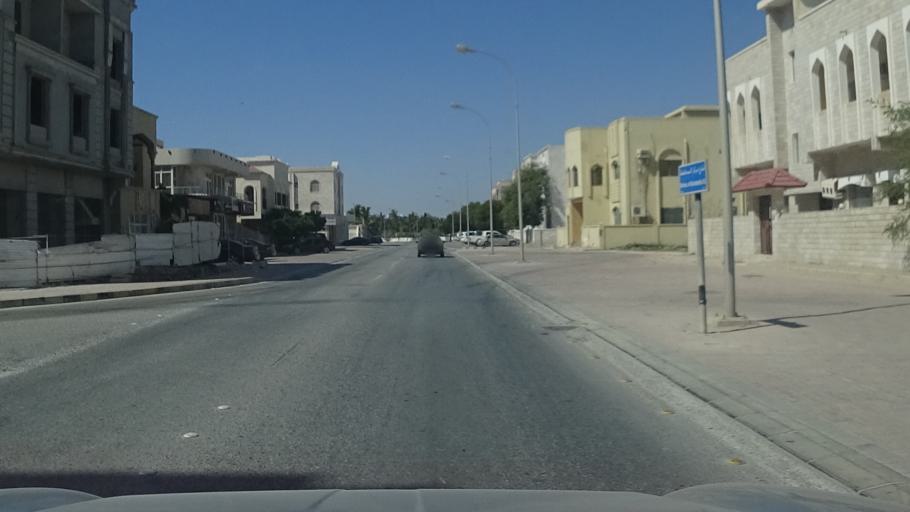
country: OM
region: Zufar
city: Salalah
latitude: 17.0210
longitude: 54.0780
